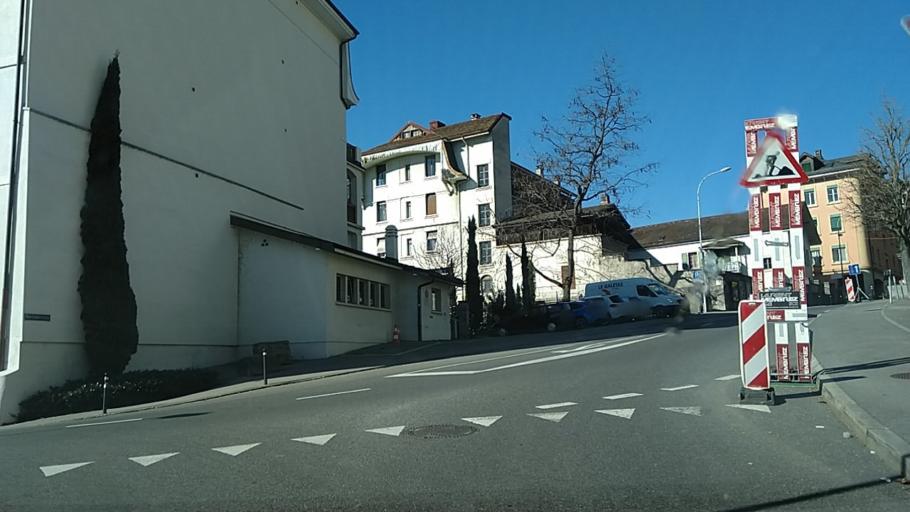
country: CH
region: Vaud
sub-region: Riviera-Pays-d'Enhaut District
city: Montreux
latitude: 46.4328
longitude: 6.9135
